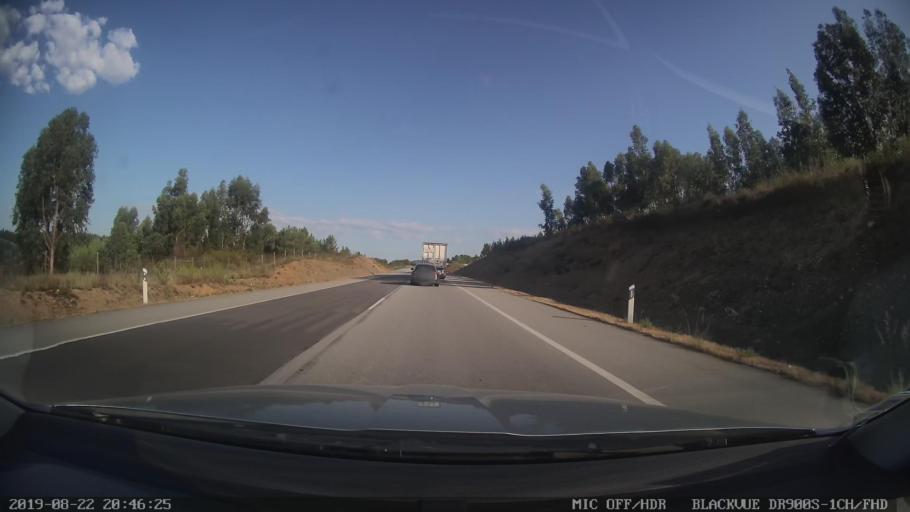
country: PT
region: Castelo Branco
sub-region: Proenca-A-Nova
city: Proenca-a-Nova
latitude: 39.7264
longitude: -7.8763
